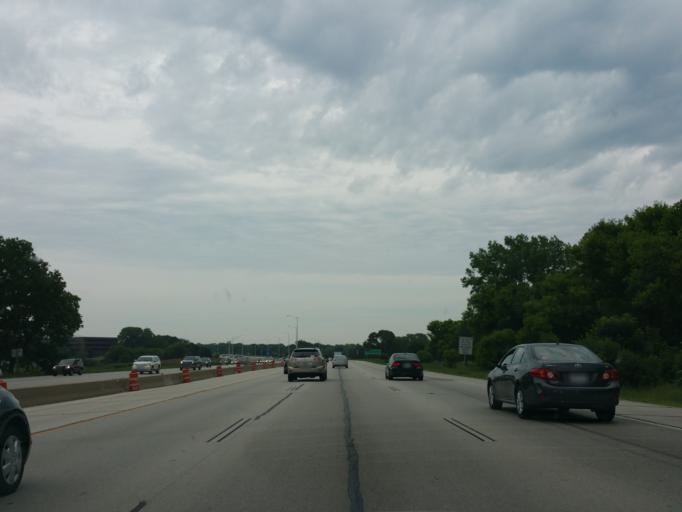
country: US
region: Wisconsin
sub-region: Waukesha County
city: Brookfield
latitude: 43.0260
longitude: -88.1188
